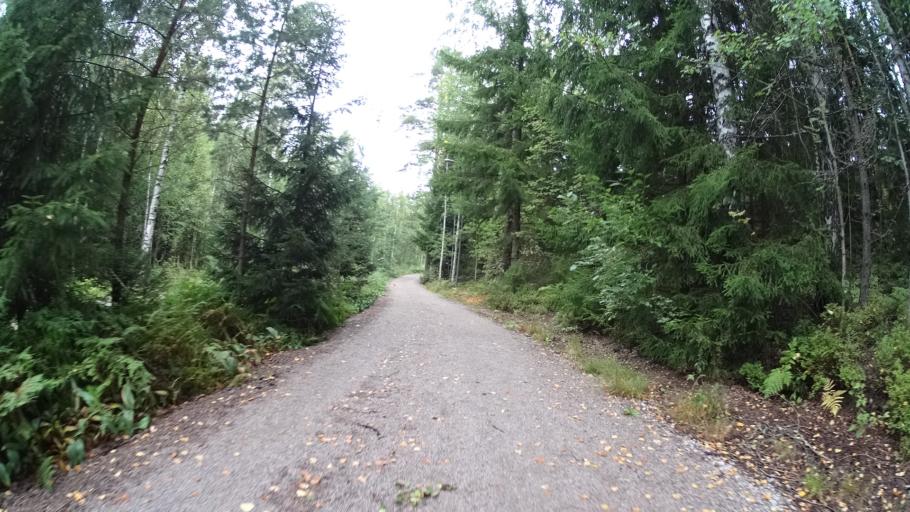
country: FI
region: Uusimaa
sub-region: Helsinki
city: Kauniainen
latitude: 60.1828
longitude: 24.7251
